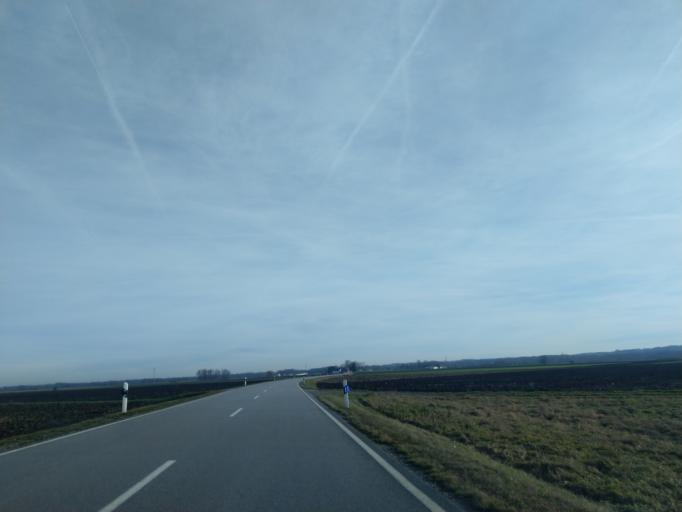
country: DE
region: Bavaria
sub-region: Lower Bavaria
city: Wallersdorf
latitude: 48.7235
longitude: 12.7861
